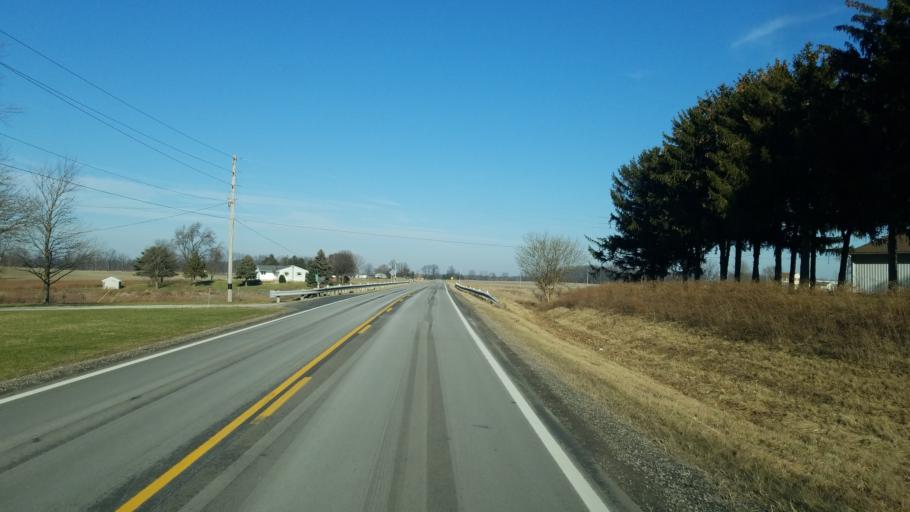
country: US
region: Ohio
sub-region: Huron County
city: Norwalk
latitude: 41.1760
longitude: -82.6428
